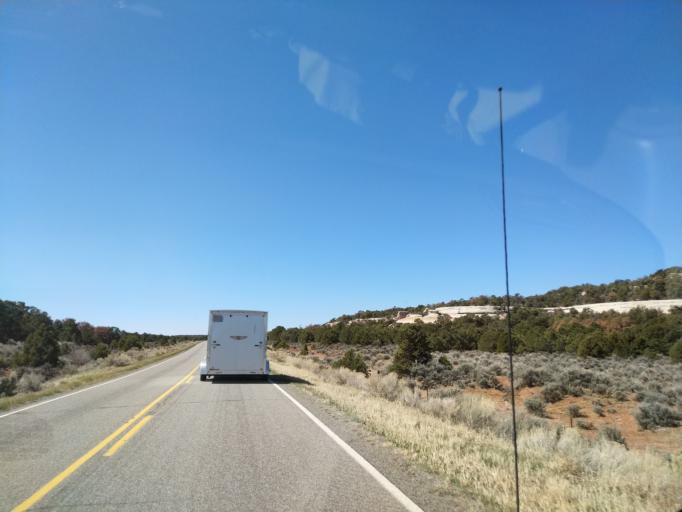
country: US
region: Colorado
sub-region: Mesa County
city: Redlands
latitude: 39.0085
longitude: -108.6840
